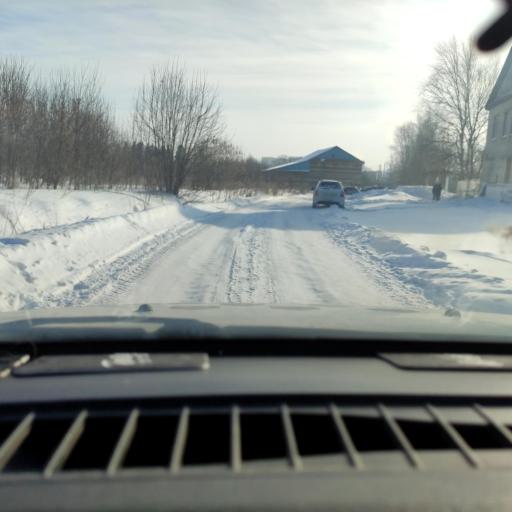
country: RU
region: Perm
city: Gamovo
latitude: 57.8766
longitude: 56.0837
